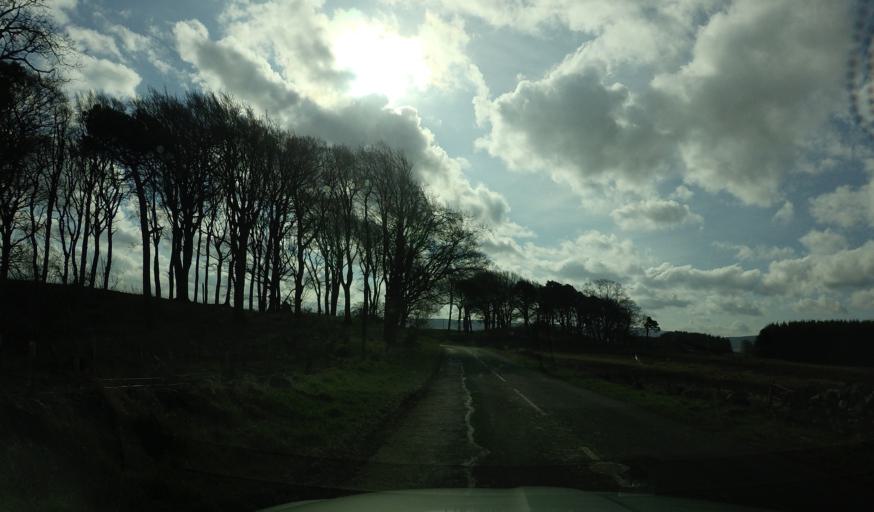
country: GB
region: Scotland
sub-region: Midlothian
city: Penicuik
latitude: 55.8021
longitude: -3.1715
